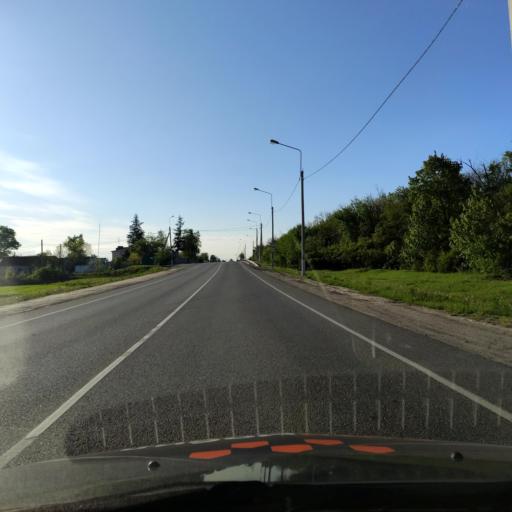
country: RU
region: Lipetsk
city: Yelets
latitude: 52.5588
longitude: 38.6909
